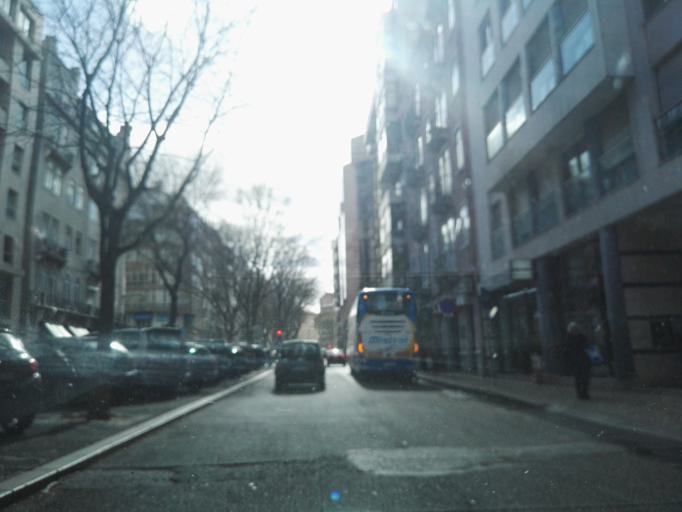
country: PT
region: Lisbon
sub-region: Lisbon
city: Lisbon
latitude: 38.7384
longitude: -9.1500
